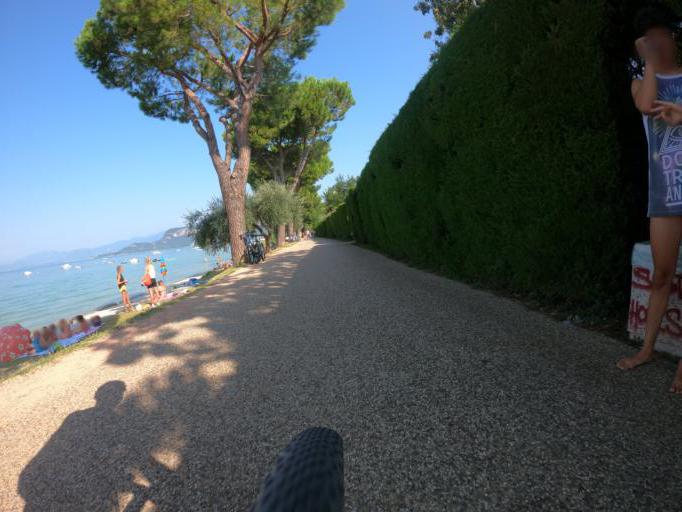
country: IT
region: Veneto
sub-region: Provincia di Verona
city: Garda
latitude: 45.5569
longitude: 10.7163
